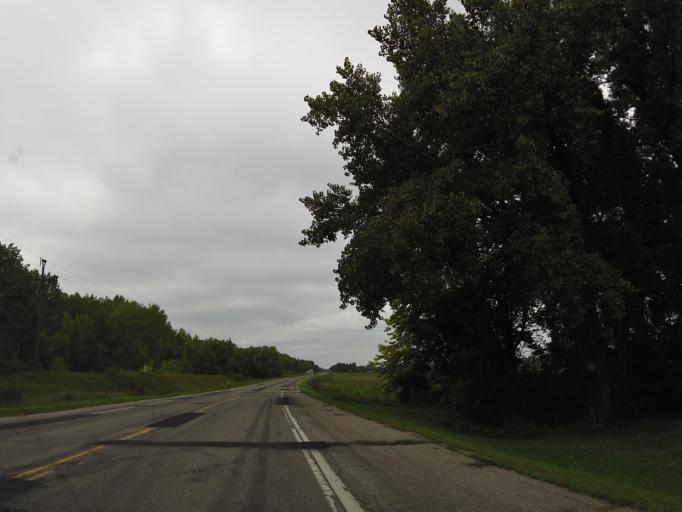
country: US
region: Minnesota
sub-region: Yellow Medicine County
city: Granite Falls
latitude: 44.8372
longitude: -95.6114
